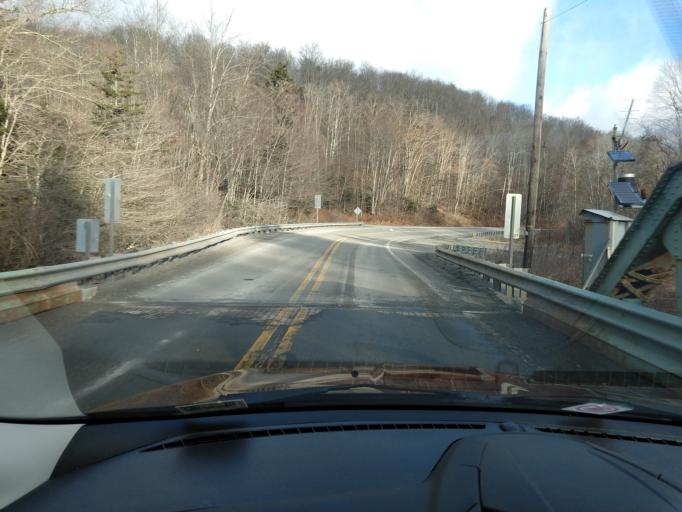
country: US
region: West Virginia
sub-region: Randolph County
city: Elkins
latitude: 38.6211
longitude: -79.8676
